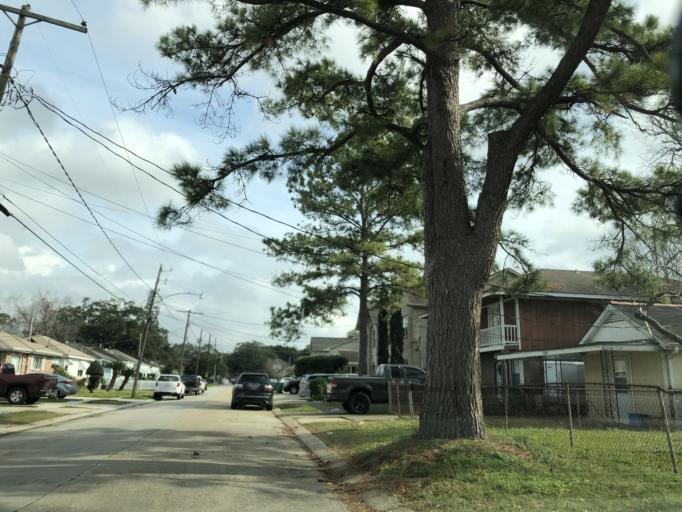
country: US
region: Louisiana
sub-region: Jefferson Parish
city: Metairie Terrace
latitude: 29.9777
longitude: -90.1688
